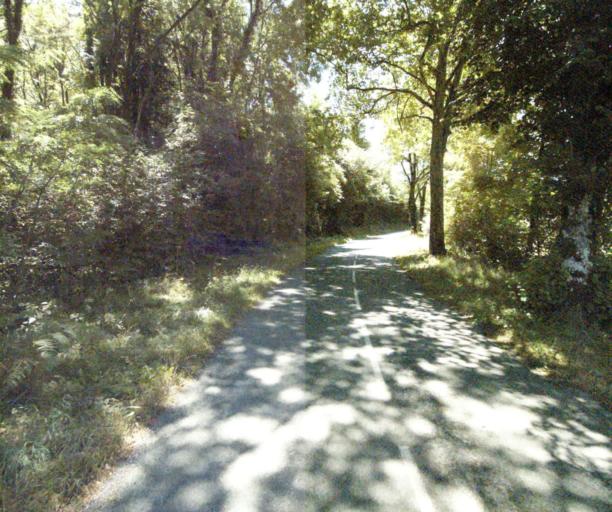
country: FR
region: Midi-Pyrenees
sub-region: Departement du Tarn
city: Dourgne
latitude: 43.4254
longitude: 2.1710
